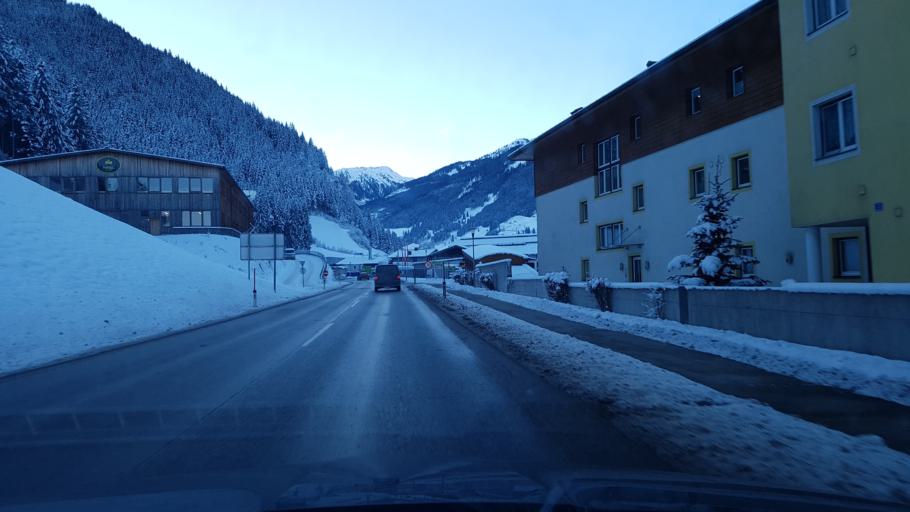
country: AT
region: Salzburg
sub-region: Politischer Bezirk Sankt Johann im Pongau
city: Huttschlag
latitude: 47.2307
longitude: 13.1990
